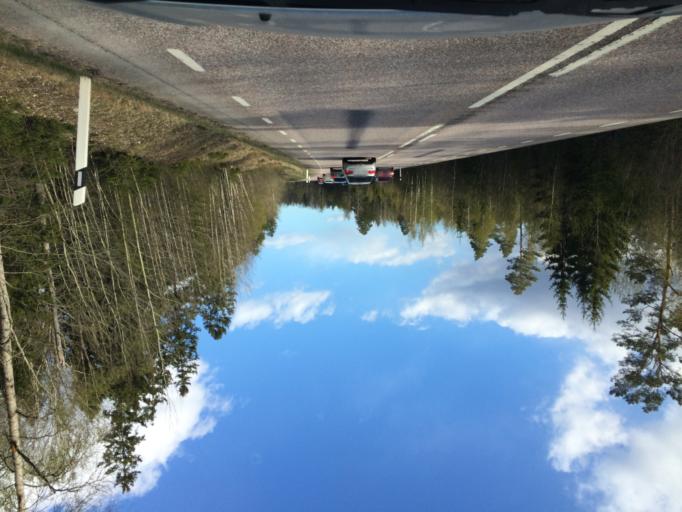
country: SE
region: Soedermanland
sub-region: Eskilstuna Kommun
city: Kvicksund
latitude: 59.5001
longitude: 16.3036
